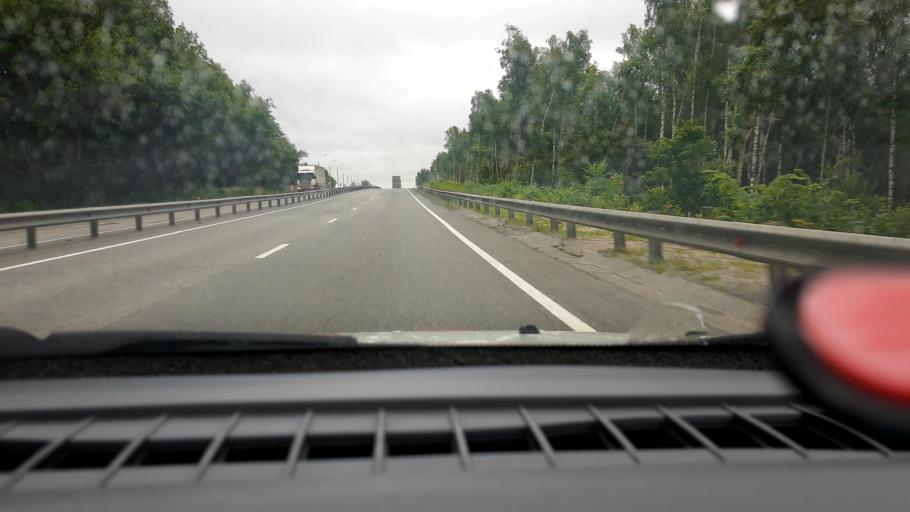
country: RU
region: Vladimir
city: Novovyazniki
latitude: 56.1891
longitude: 42.3910
